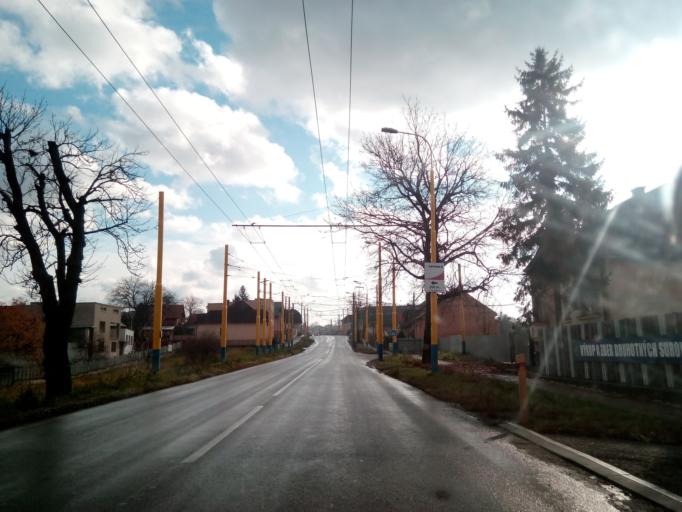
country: SK
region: Presovsky
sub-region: Okres Presov
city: Presov
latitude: 48.9796
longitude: 21.2600
